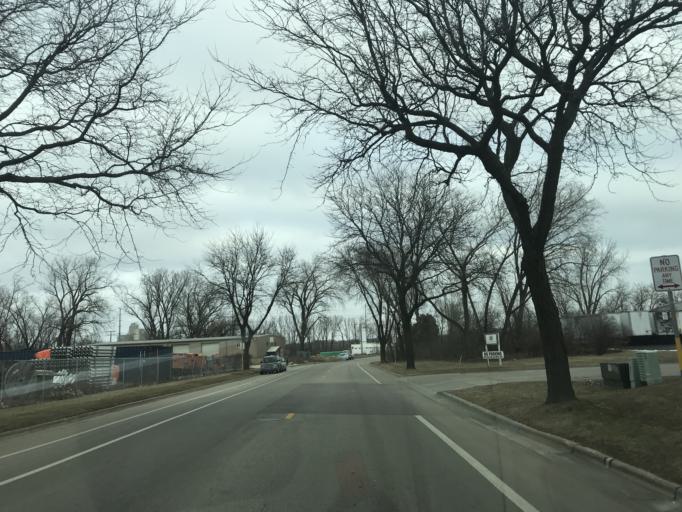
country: US
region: Wisconsin
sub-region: Dane County
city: Monona
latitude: 43.1113
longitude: -89.3100
